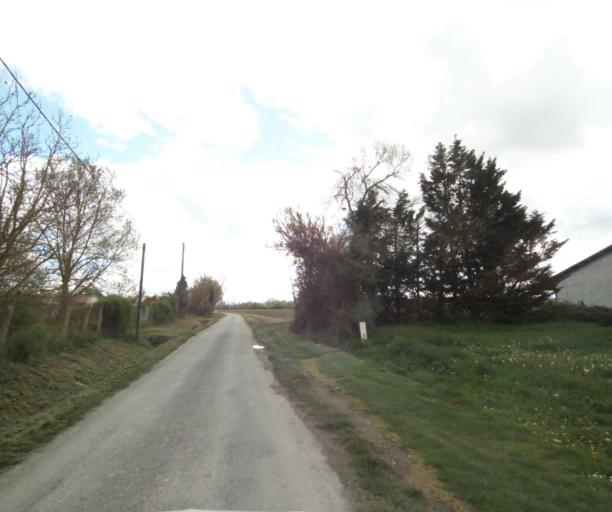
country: FR
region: Midi-Pyrenees
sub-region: Departement de l'Ariege
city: Saverdun
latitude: 43.2598
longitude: 1.5812
